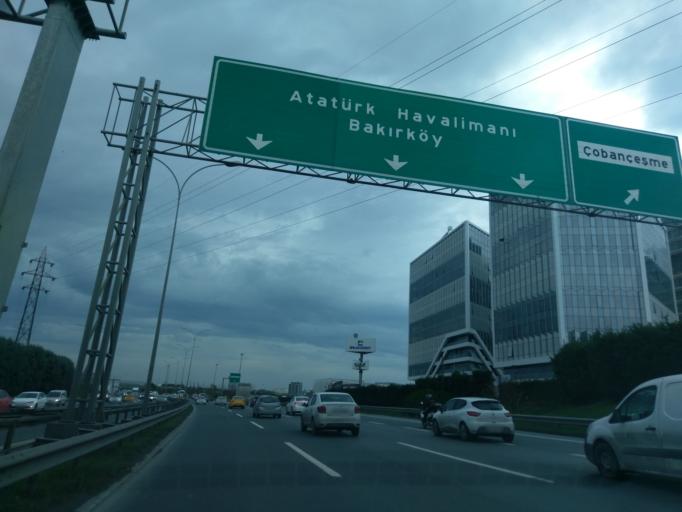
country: TR
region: Istanbul
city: Bahcelievler
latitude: 41.0030
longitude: 28.8148
